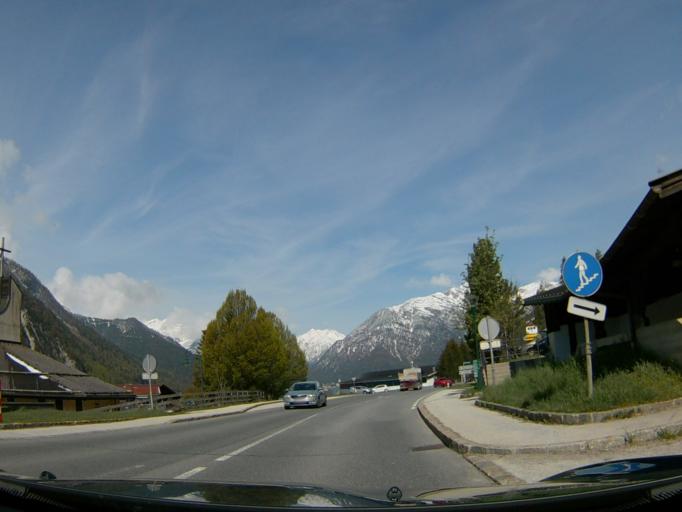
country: AT
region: Tyrol
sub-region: Politischer Bezirk Schwaz
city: Jenbach
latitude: 47.4238
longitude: 11.7515
